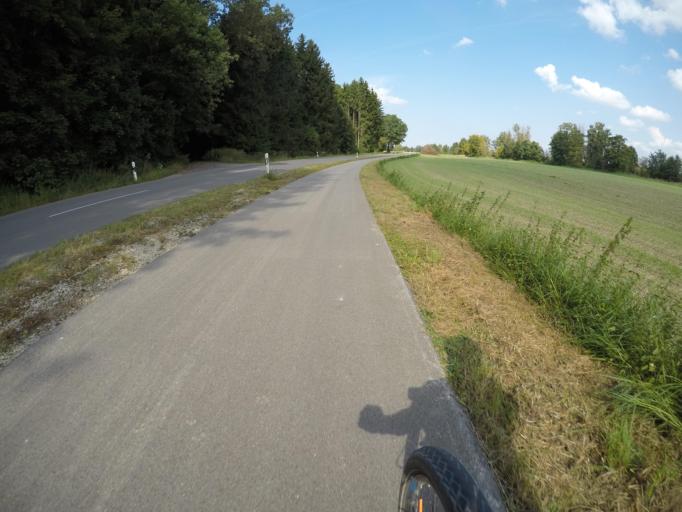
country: DE
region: Bavaria
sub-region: Swabia
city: Kuhlenthal
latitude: 48.5743
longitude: 10.8233
